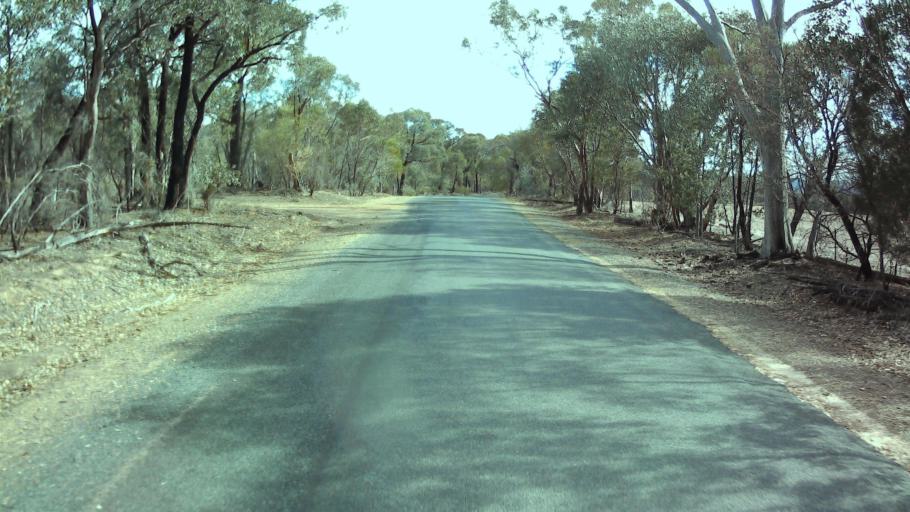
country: AU
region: New South Wales
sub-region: Weddin
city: Grenfell
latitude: -33.8737
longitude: 148.2019
